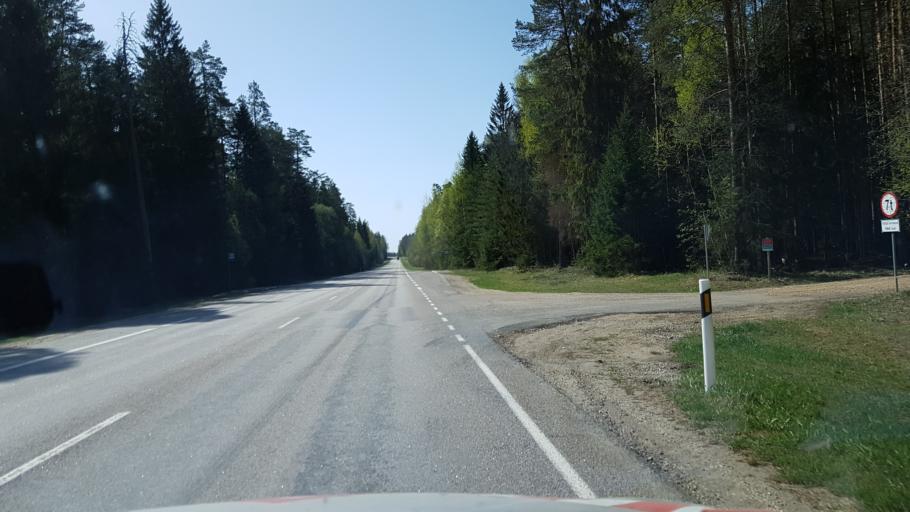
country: EE
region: Valgamaa
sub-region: Valga linn
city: Valga
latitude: 57.8532
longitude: 26.0594
